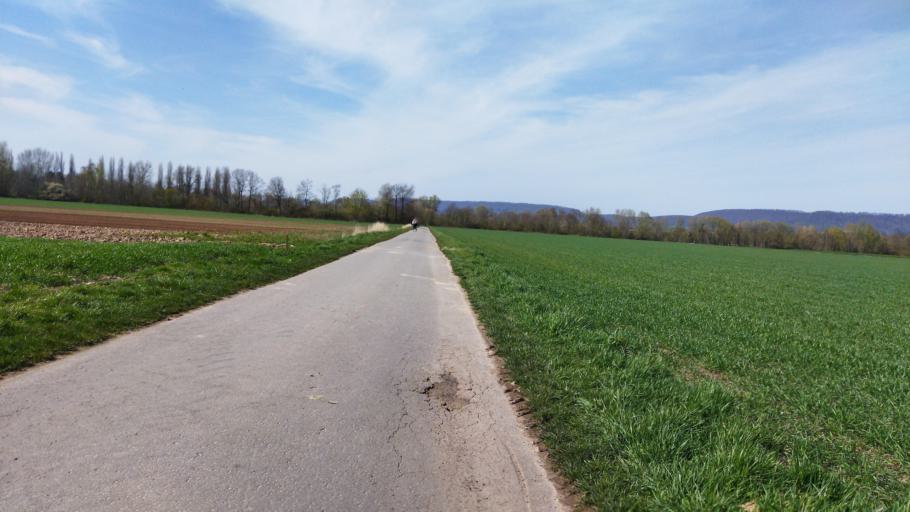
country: DE
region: Lower Saxony
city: Hessisch Oldendorf
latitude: 52.1447
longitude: 9.2826
